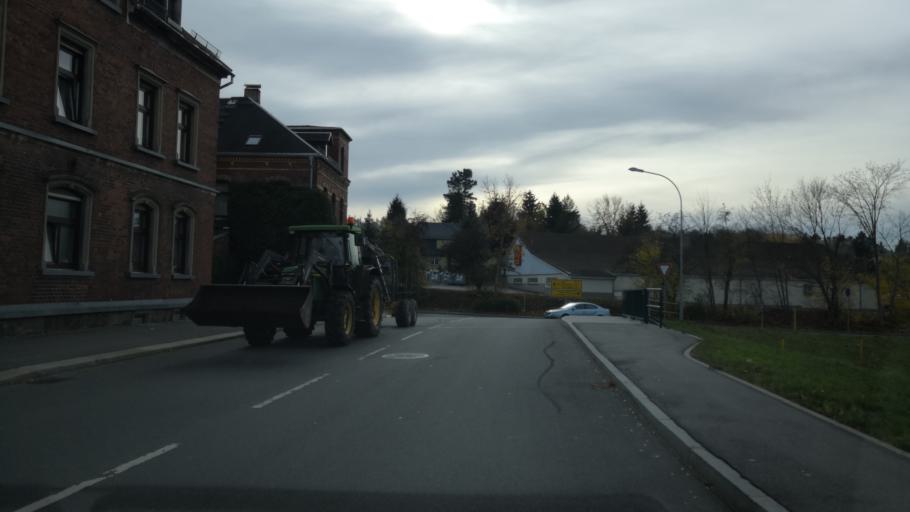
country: DE
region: Saxony
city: Rodewisch
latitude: 50.5322
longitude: 12.4202
